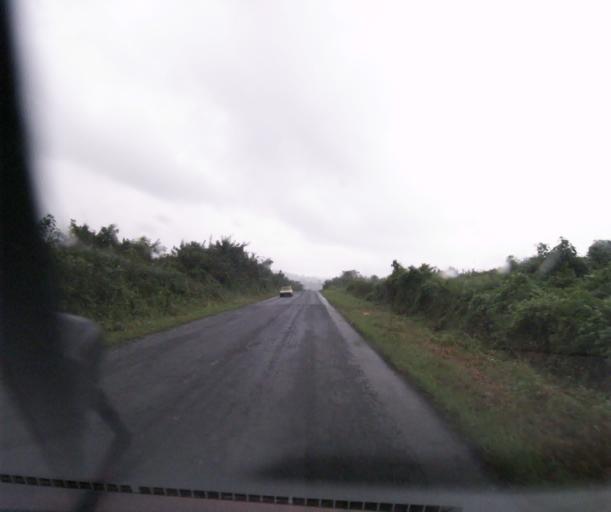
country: CM
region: South-West Province
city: Idenao
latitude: 4.1880
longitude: 9.0034
